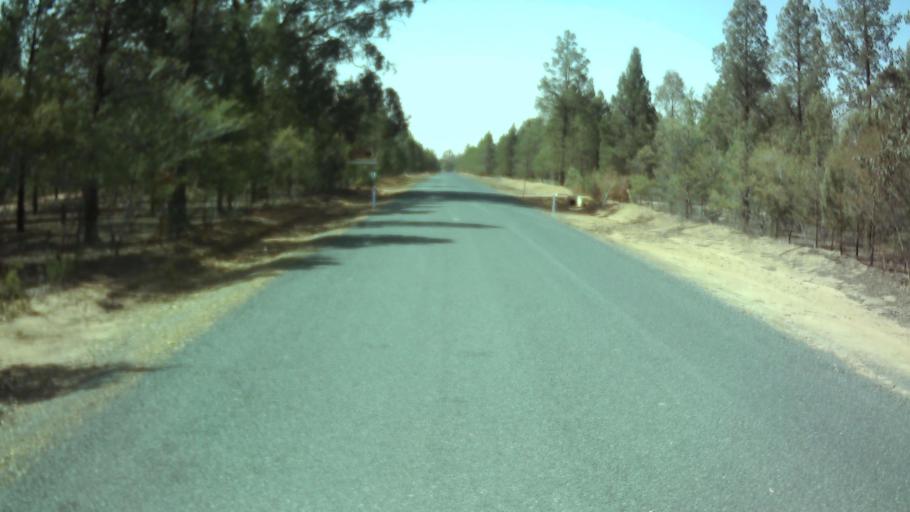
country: AU
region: New South Wales
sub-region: Weddin
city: Grenfell
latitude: -33.9069
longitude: 147.9196
